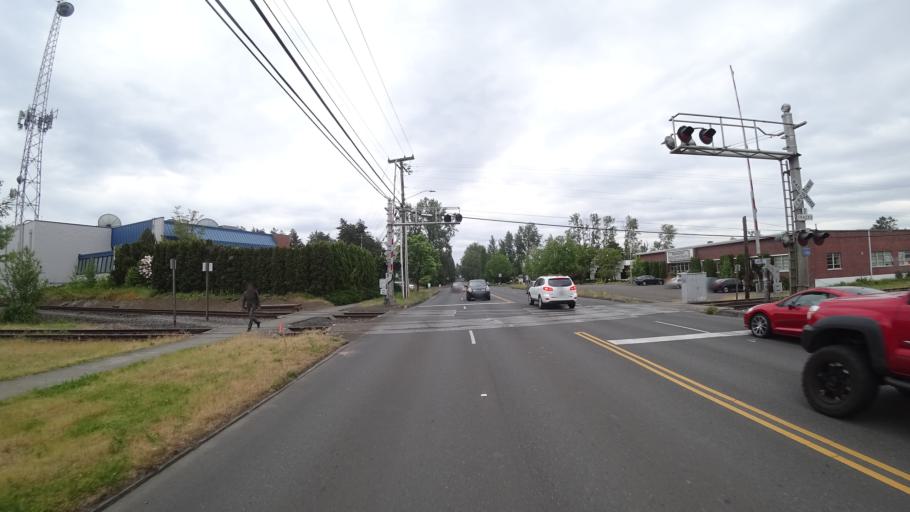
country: US
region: Oregon
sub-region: Washington County
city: Raleigh Hills
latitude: 45.4822
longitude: -122.7827
